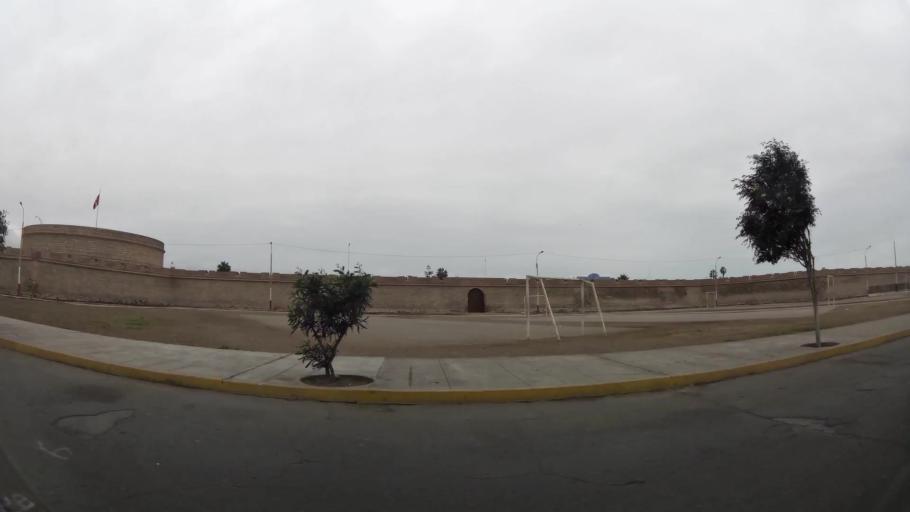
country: PE
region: Callao
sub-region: Callao
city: Callao
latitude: -12.0632
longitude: -77.1512
